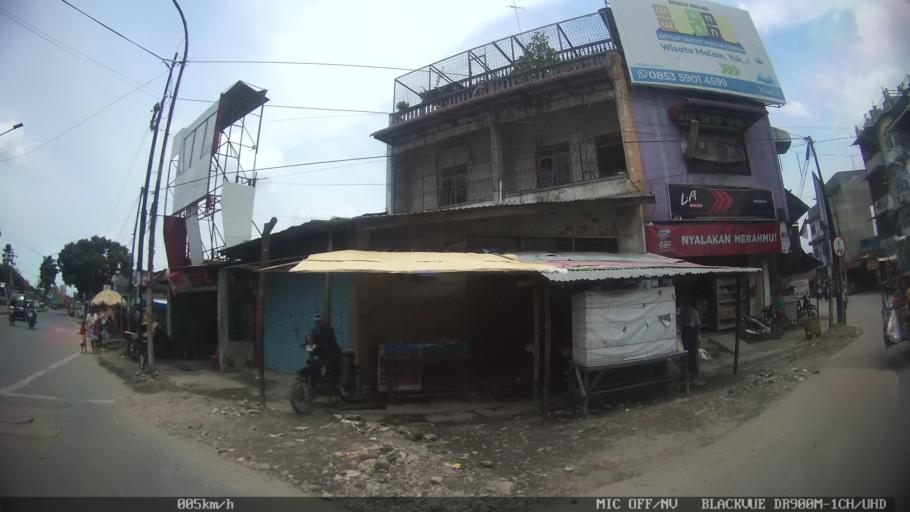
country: ID
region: North Sumatra
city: Labuhan Deli
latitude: 3.6965
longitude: 98.6734
